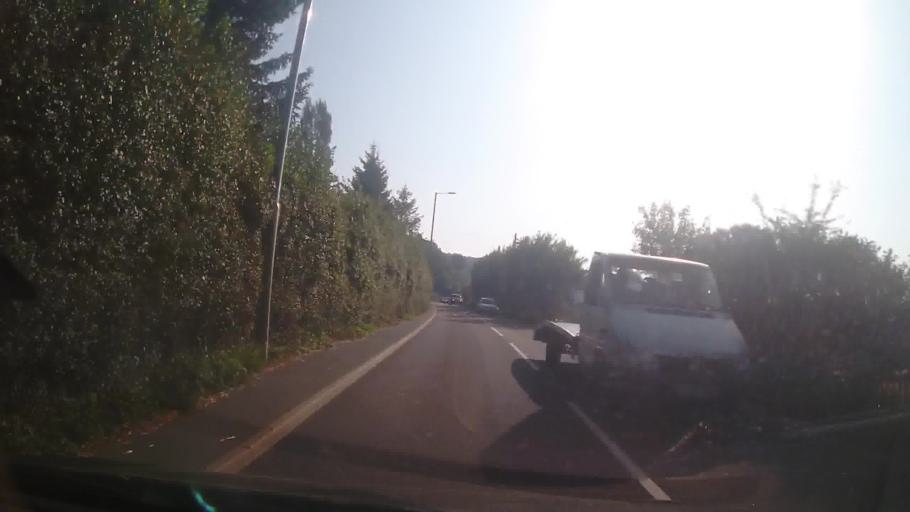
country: GB
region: England
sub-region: Shropshire
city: Bridgnorth
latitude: 52.5219
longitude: -2.3971
